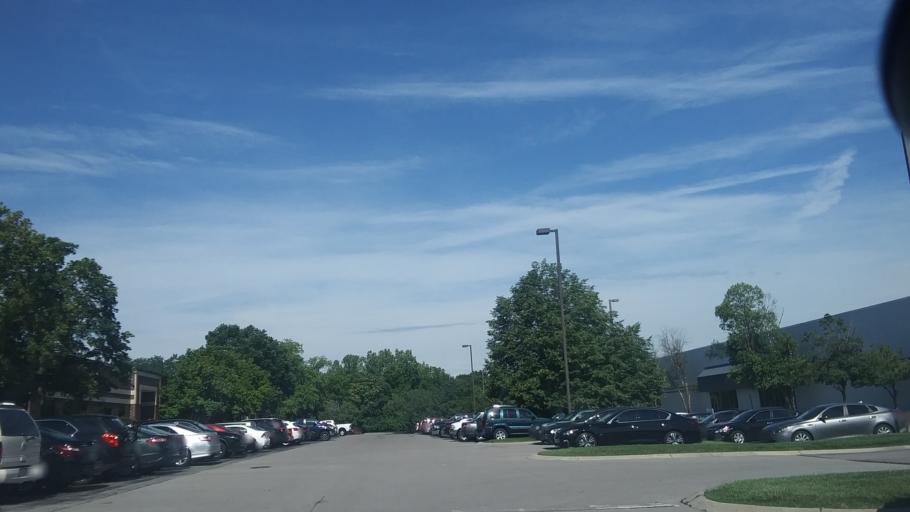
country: US
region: Tennessee
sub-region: Davidson County
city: Oak Hill
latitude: 36.0771
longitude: -86.6960
